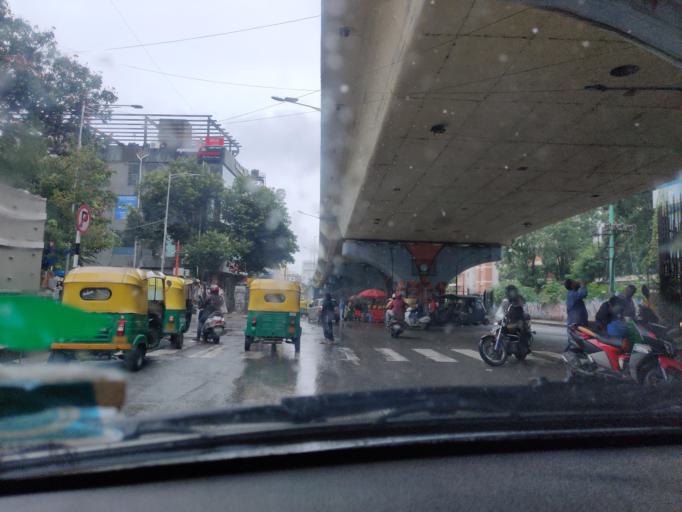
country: IN
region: Karnataka
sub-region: Bangalore Urban
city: Bangalore
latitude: 13.0248
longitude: 77.6315
